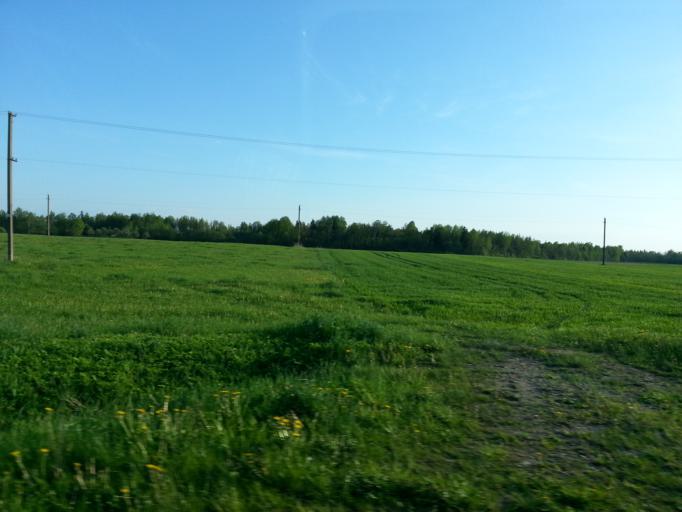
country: LT
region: Vilnius County
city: Ukmerge
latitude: 55.4196
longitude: 24.5754
